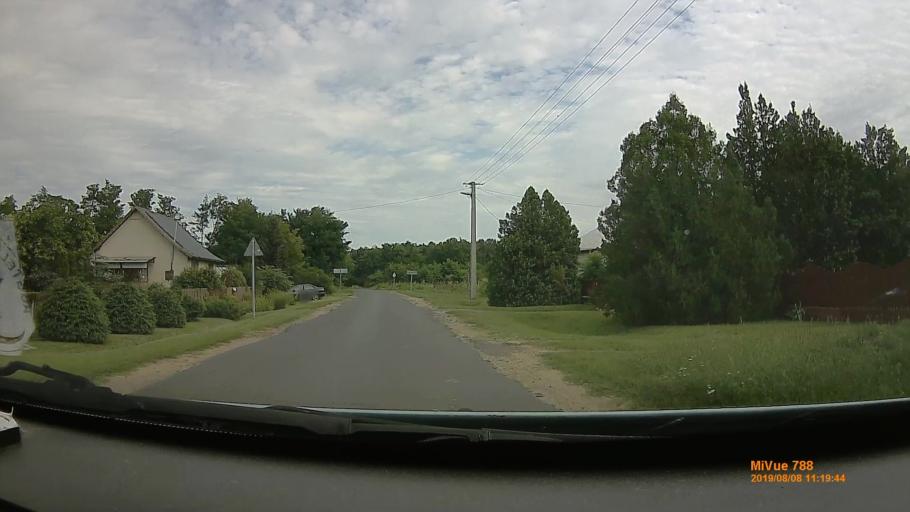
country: HU
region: Szabolcs-Szatmar-Bereg
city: Balkany
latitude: 47.7474
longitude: 21.8409
